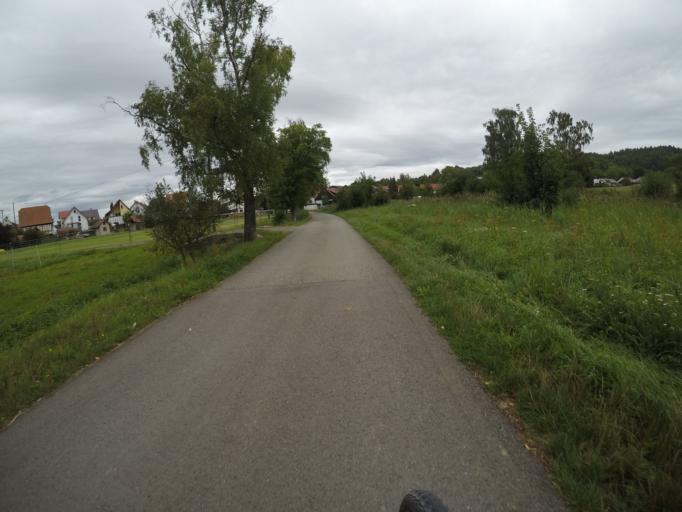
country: DE
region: Baden-Wuerttemberg
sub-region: Regierungsbezirk Stuttgart
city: Gartringen
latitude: 48.6243
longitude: 8.9249
